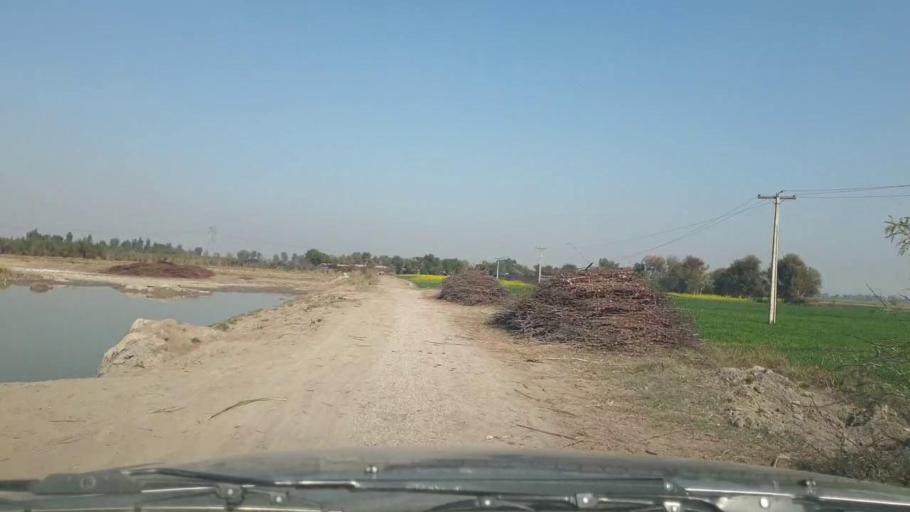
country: PK
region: Sindh
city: Mirpur Mathelo
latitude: 28.0453
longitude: 69.5620
